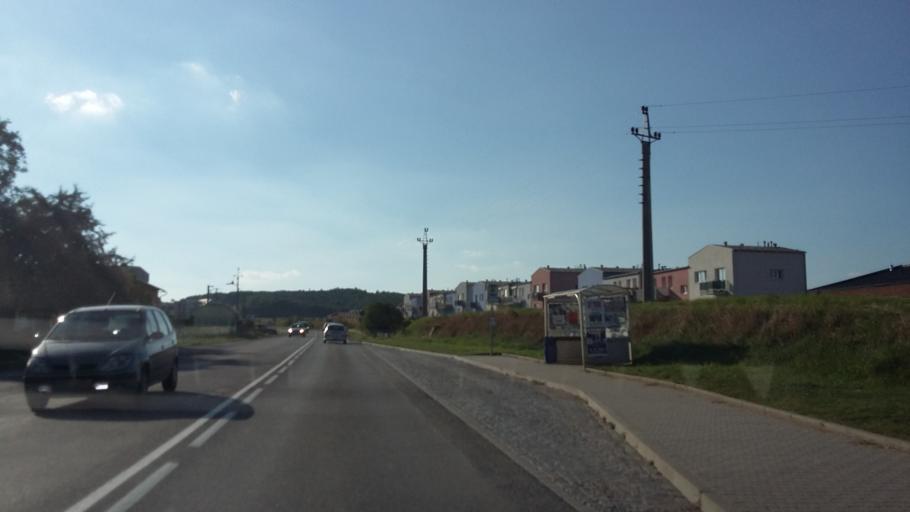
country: CZ
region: South Moravian
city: Troubsko
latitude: 49.1816
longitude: 16.4910
